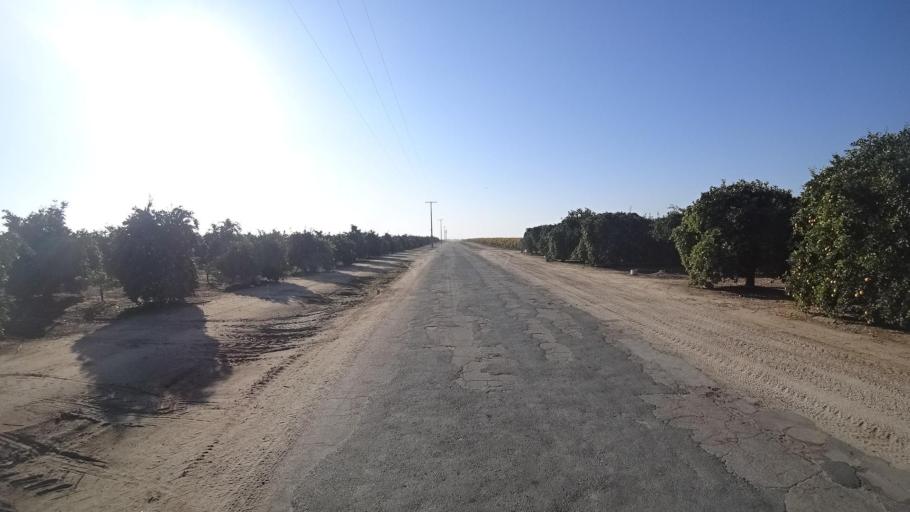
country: US
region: California
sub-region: Tulare County
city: Richgrove
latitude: 35.7728
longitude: -119.1607
